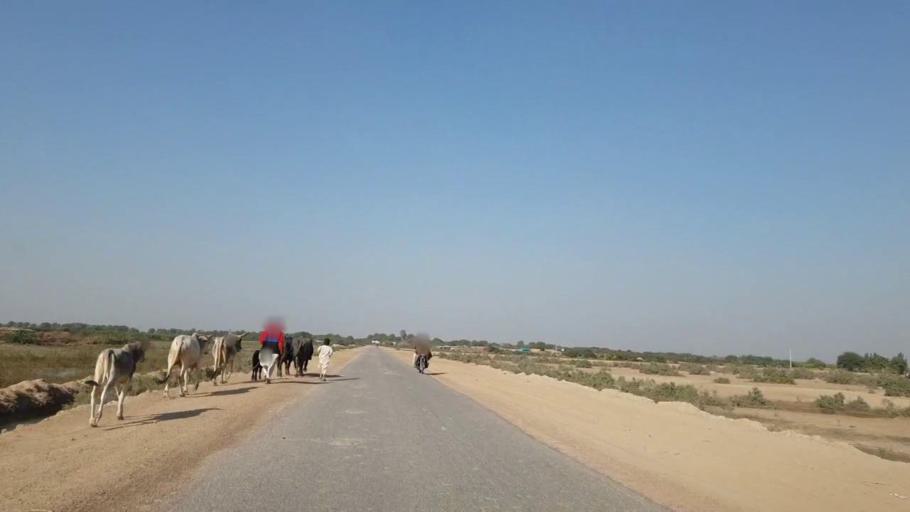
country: PK
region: Sindh
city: Digri
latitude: 25.1168
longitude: 69.1081
